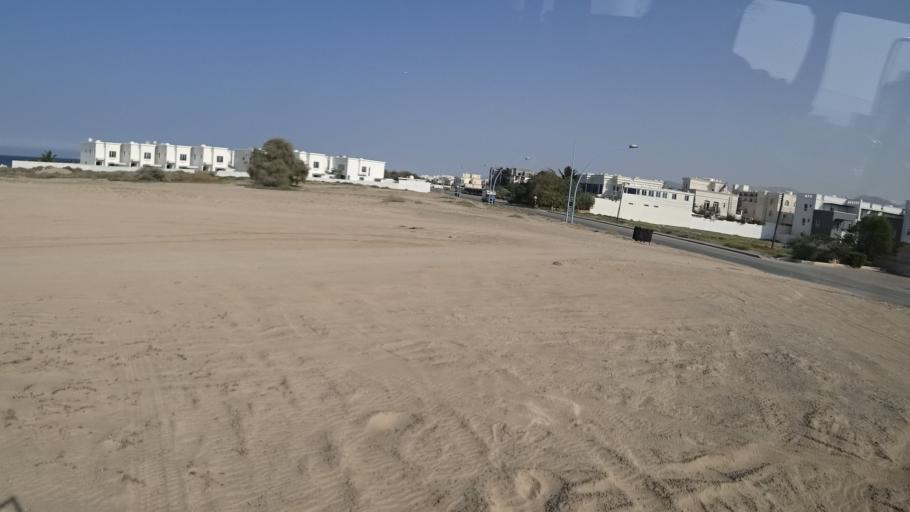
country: OM
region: Muhafazat Masqat
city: Bawshar
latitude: 23.6043
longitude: 58.3547
